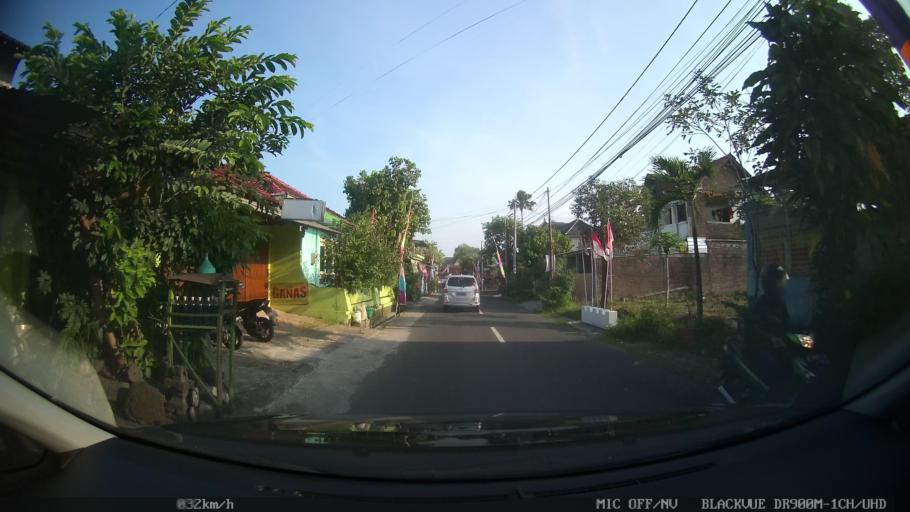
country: ID
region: Daerah Istimewa Yogyakarta
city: Depok
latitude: -7.7762
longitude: 110.4046
